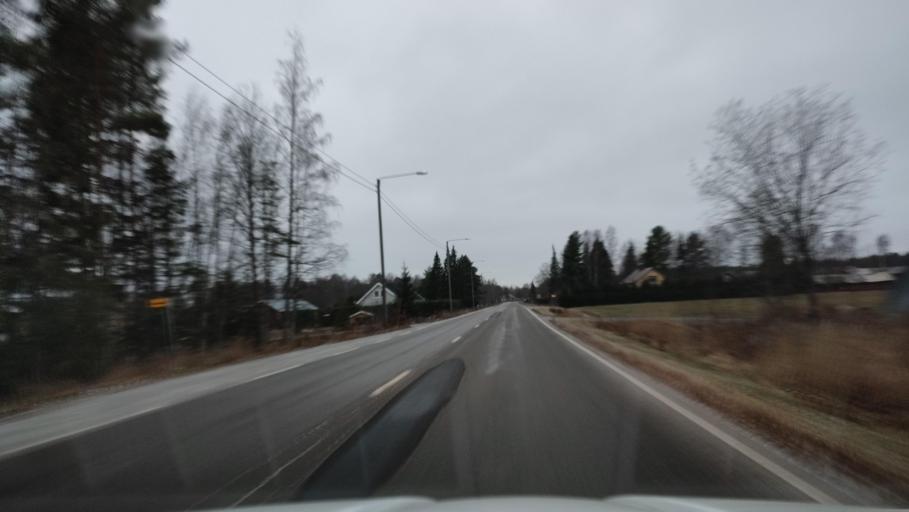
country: FI
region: Southern Ostrobothnia
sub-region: Suupohja
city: Karijoki
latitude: 62.2408
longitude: 21.5892
